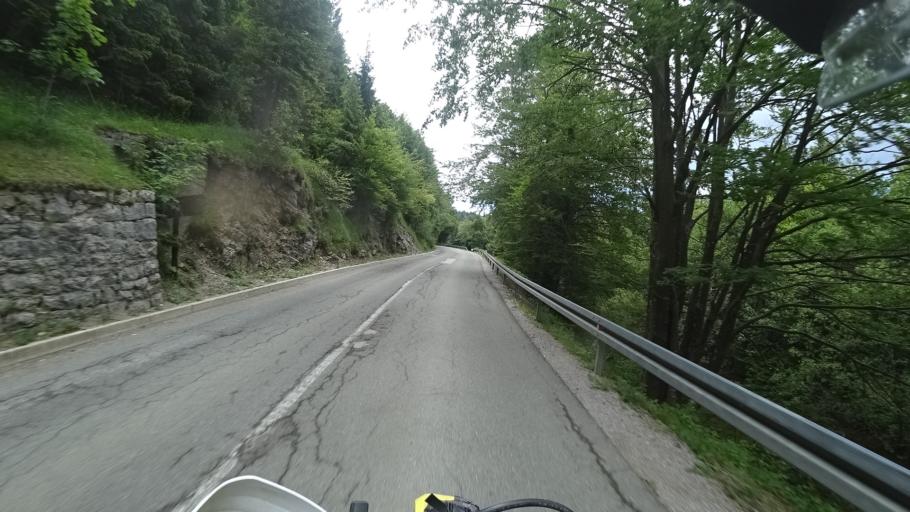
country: HR
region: Primorsko-Goranska
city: Hreljin
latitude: 45.3253
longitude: 14.7044
